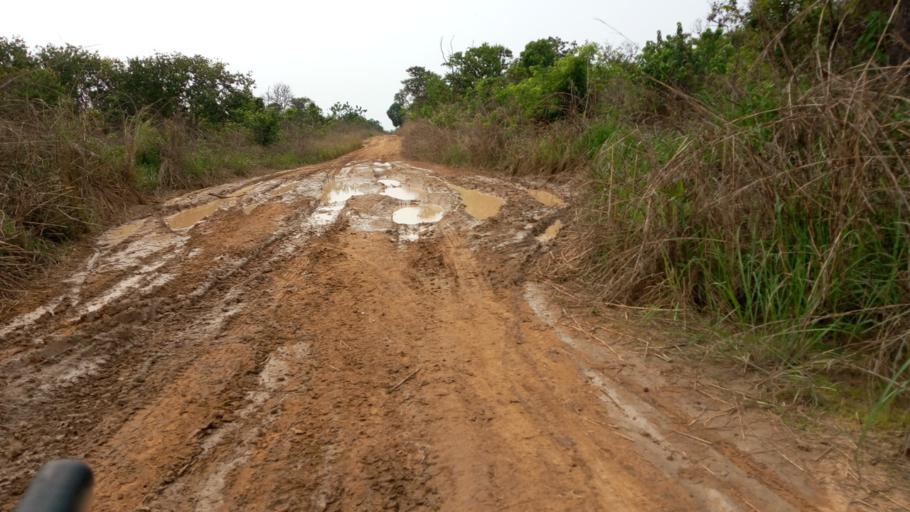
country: CD
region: Bandundu
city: Bandundu
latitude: -3.4668
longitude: 17.7742
